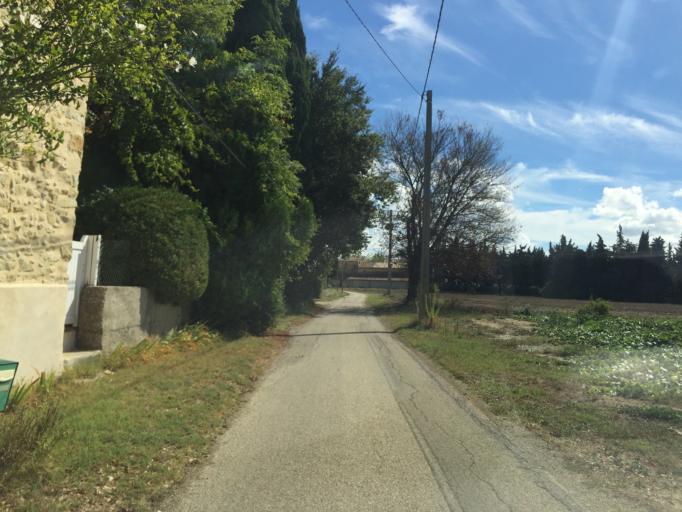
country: FR
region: Provence-Alpes-Cote d'Azur
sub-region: Departement du Vaucluse
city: Caderousse
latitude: 44.1241
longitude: 4.7360
